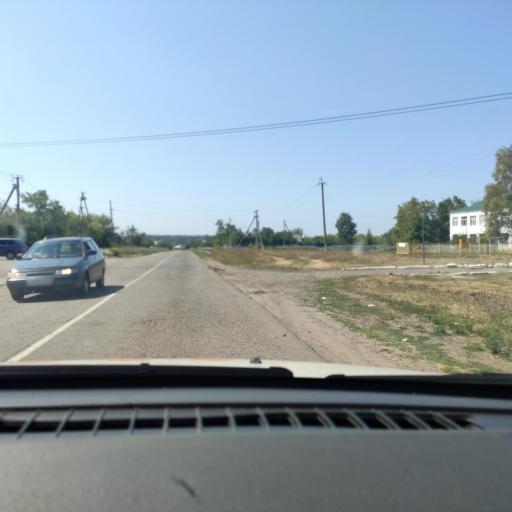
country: RU
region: Voronezj
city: Imeni Pervogo Maya
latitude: 50.7183
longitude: 39.3832
